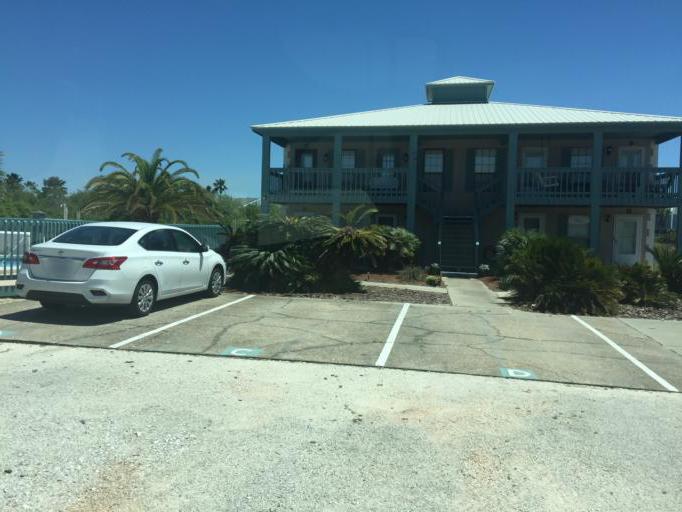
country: US
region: Florida
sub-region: Bay County
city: Laguna Beach
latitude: 30.2582
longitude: -85.9653
